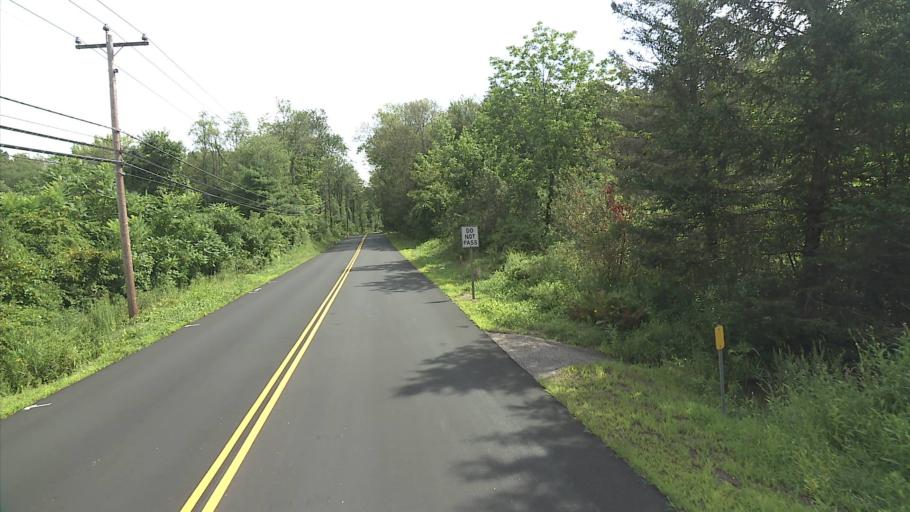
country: US
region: Connecticut
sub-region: Windham County
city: South Woodstock
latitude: 41.9529
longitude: -72.0530
